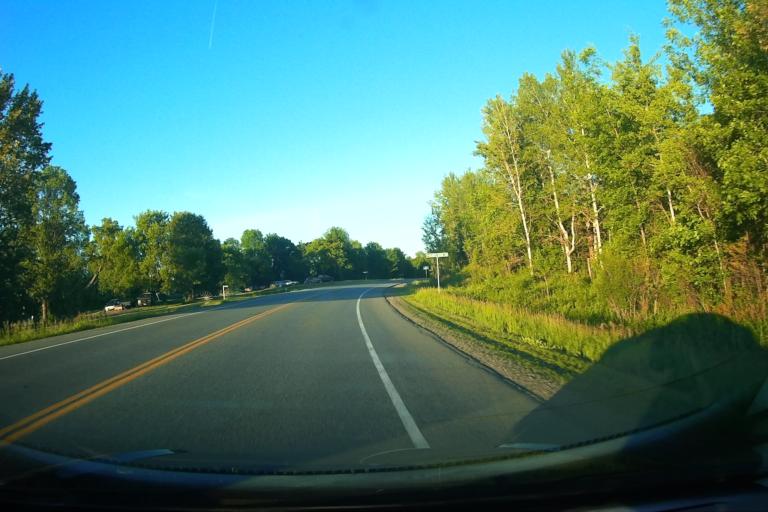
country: CA
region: Ontario
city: Prescott
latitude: 45.0595
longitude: -75.5216
